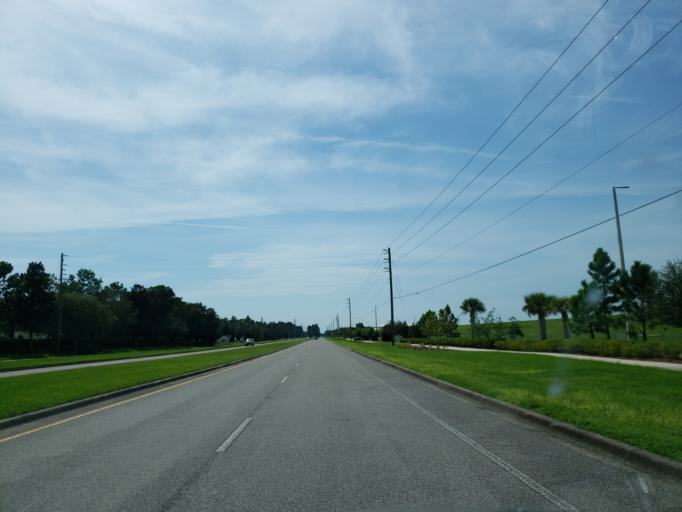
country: US
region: Florida
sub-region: Pasco County
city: Wesley Chapel
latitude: 28.2734
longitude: -82.3132
